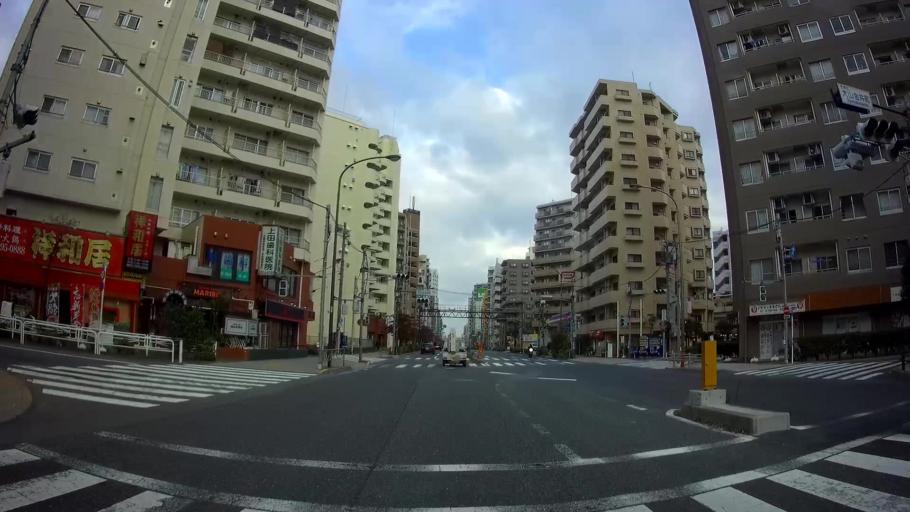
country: JP
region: Tokyo
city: Tokyo
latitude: 35.7446
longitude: 139.7024
